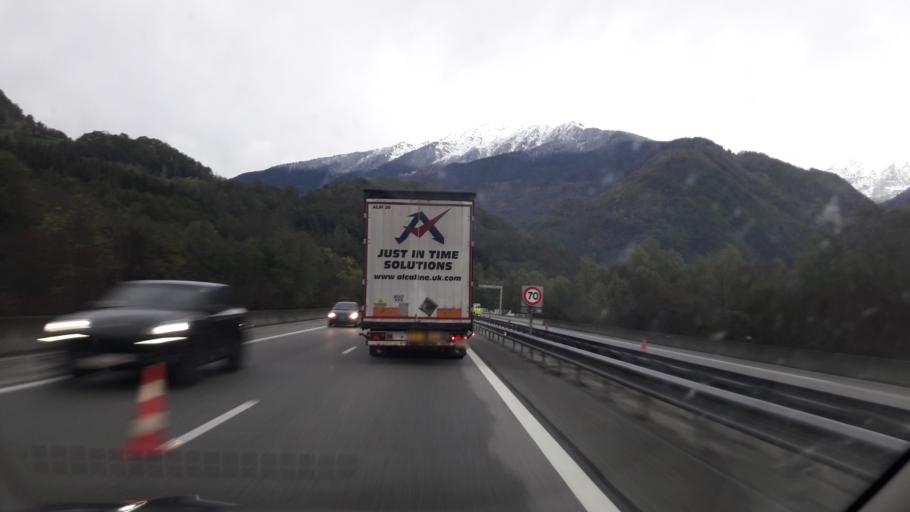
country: FR
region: Rhone-Alpes
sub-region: Departement de la Savoie
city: Aiton
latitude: 45.5049
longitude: 6.3028
